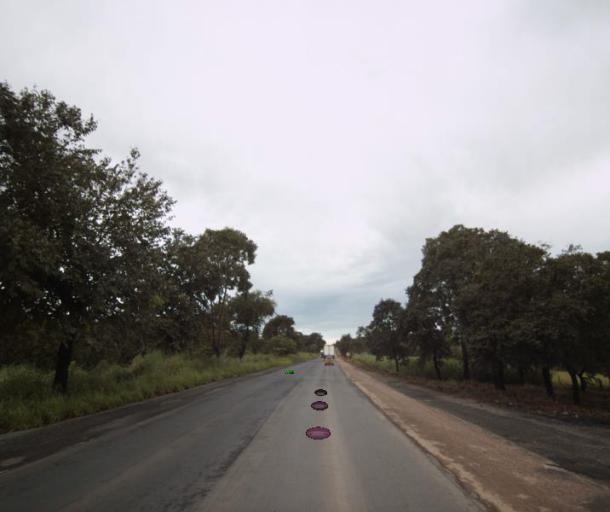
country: BR
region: Goias
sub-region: Porangatu
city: Porangatu
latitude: -13.7068
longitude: -49.0210
